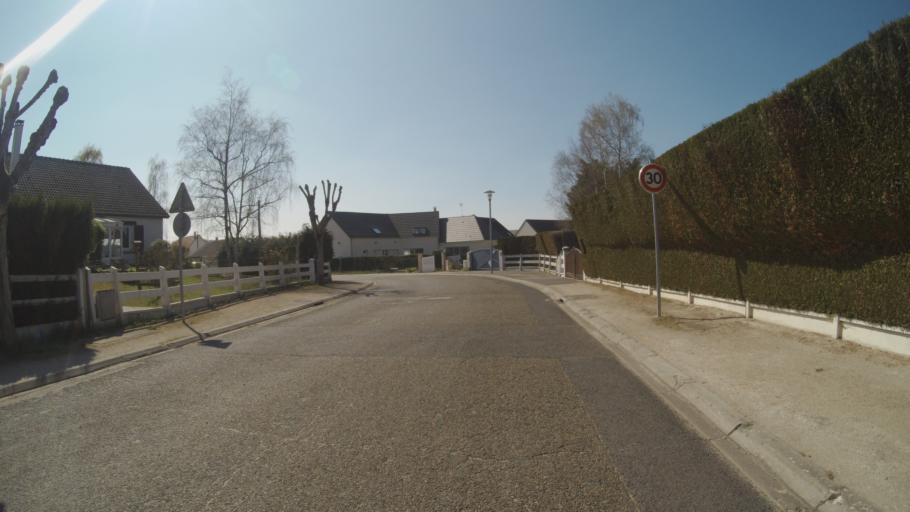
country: FR
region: Centre
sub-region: Departement du Loiret
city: Chanteau
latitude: 47.9639
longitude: 1.9677
